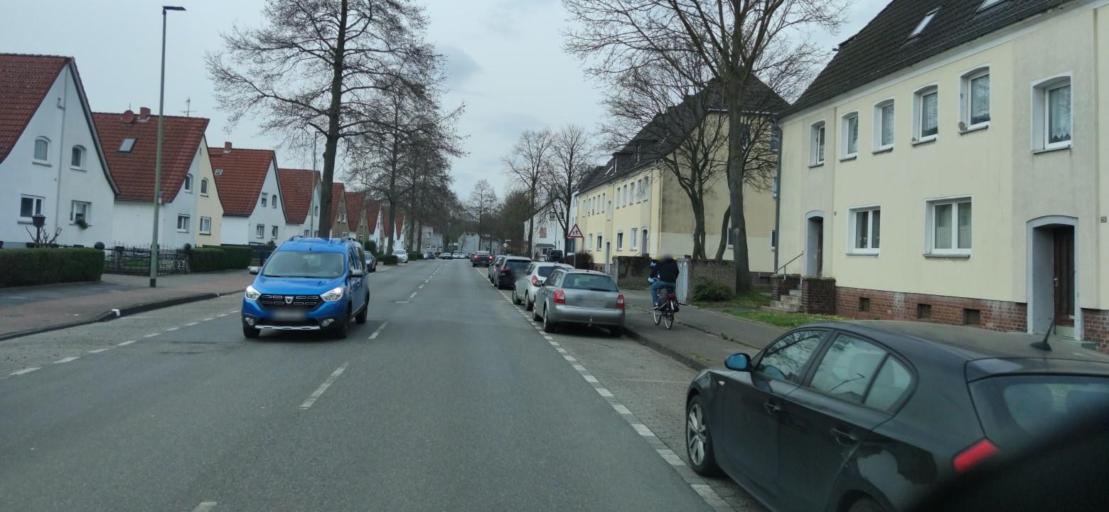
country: DE
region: North Rhine-Westphalia
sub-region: Regierungsbezirk Dusseldorf
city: Dinslaken
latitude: 51.5374
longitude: 6.7313
